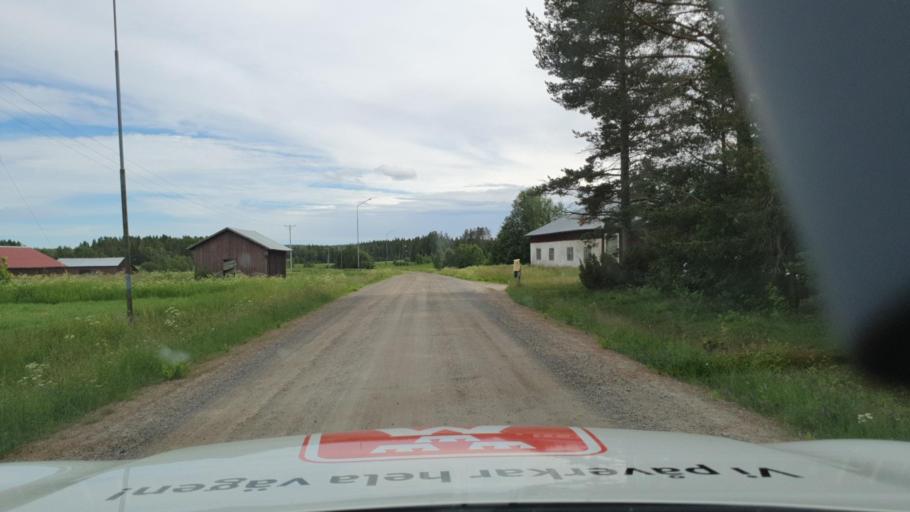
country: SE
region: Vaesterbotten
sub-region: Skelleftea Kommun
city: Burea
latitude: 64.3600
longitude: 21.0882
